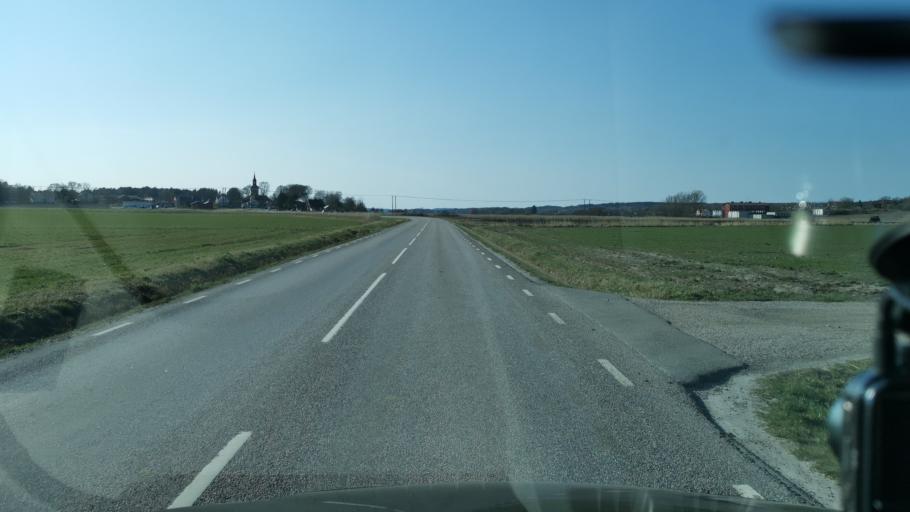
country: SE
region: Vaestra Goetaland
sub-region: Kungalvs Kommun
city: Kode
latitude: 57.9401
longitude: 11.8294
